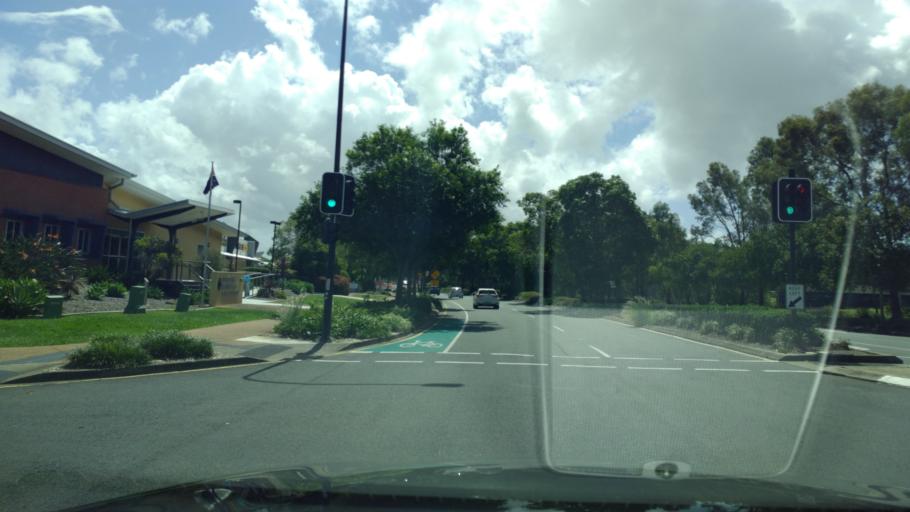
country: AU
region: Queensland
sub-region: Moreton Bay
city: Mango Hill
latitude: -27.2385
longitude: 153.0234
